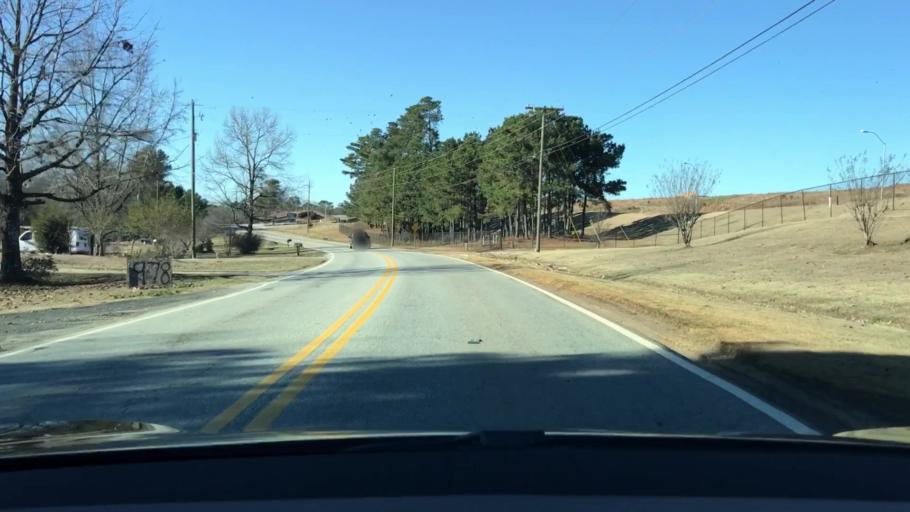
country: US
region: Georgia
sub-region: Barrow County
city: Winder
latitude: 33.9669
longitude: -83.7742
